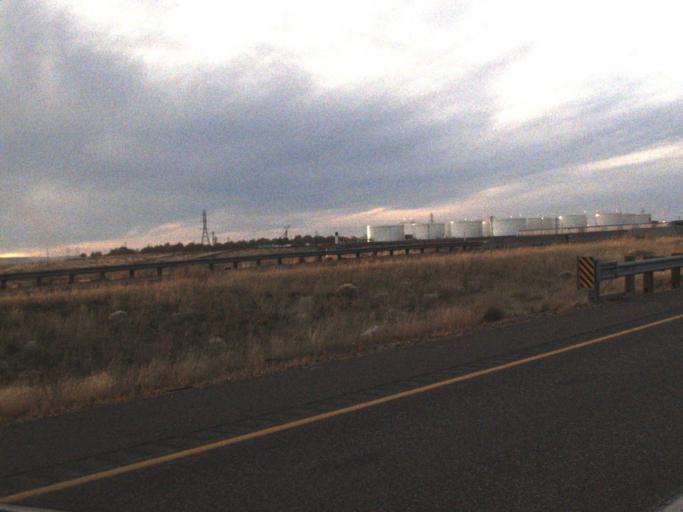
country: US
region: Washington
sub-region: Walla Walla County
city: Burbank
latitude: 46.2137
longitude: -119.0193
